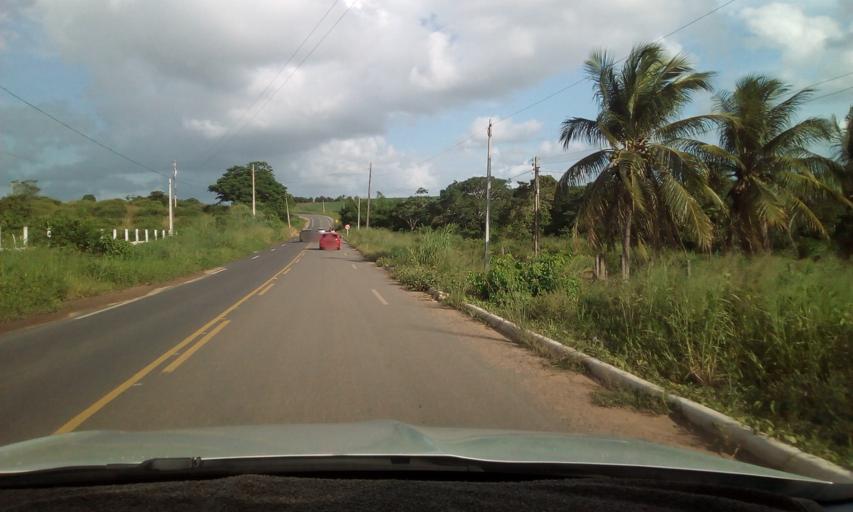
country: BR
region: Paraiba
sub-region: Mamanguape
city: Mamanguape
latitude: -6.8089
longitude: -35.1955
